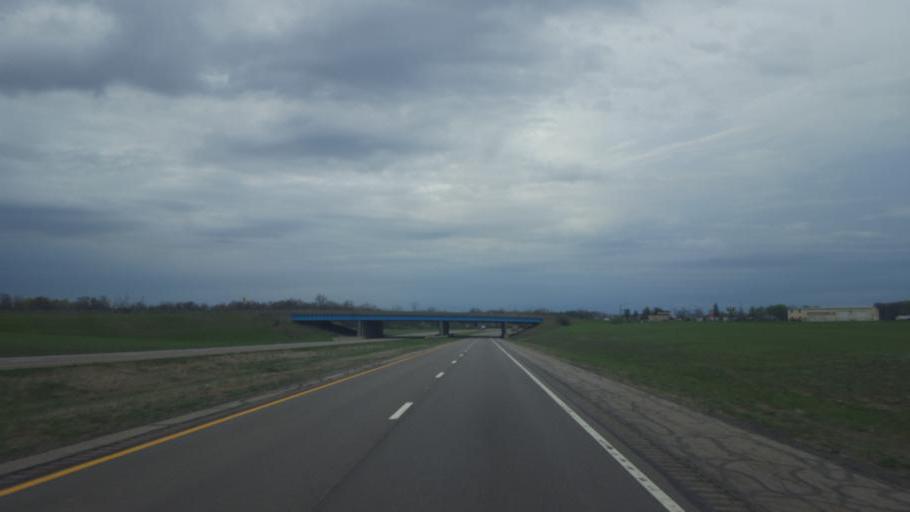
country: US
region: Ohio
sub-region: Richland County
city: Ontario
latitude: 40.7783
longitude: -82.6609
